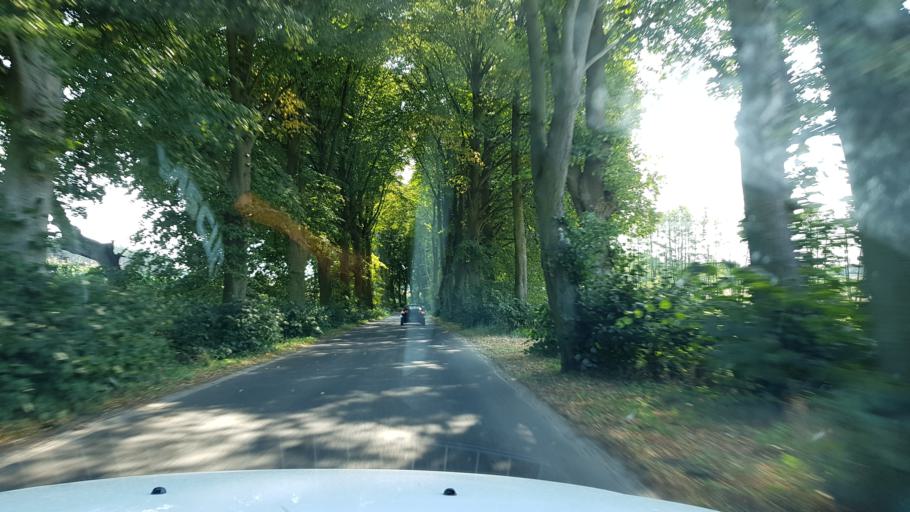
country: PL
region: West Pomeranian Voivodeship
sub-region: Powiat gryfinski
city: Chojna
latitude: 52.9577
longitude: 14.4912
